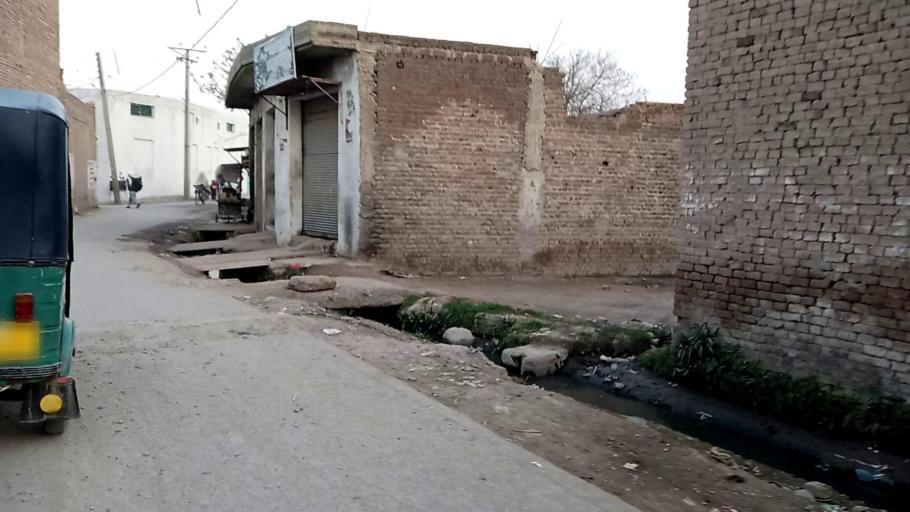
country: PK
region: Khyber Pakhtunkhwa
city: Peshawar
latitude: 34.0313
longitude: 71.4938
